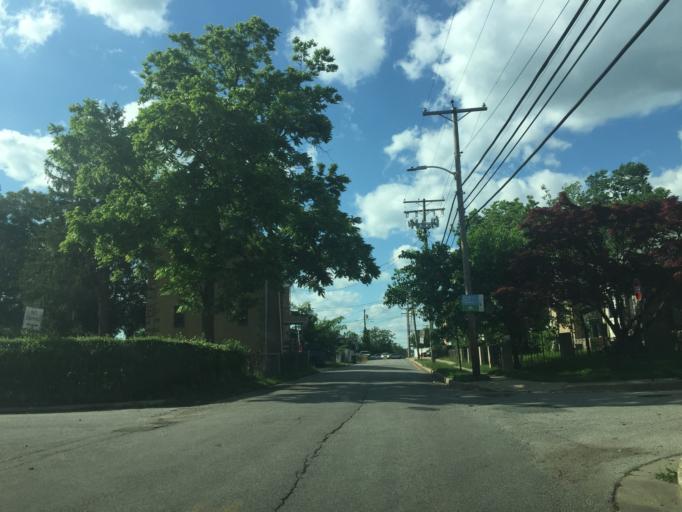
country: US
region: Maryland
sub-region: Baltimore County
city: Lochearn
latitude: 39.3509
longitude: -76.6695
